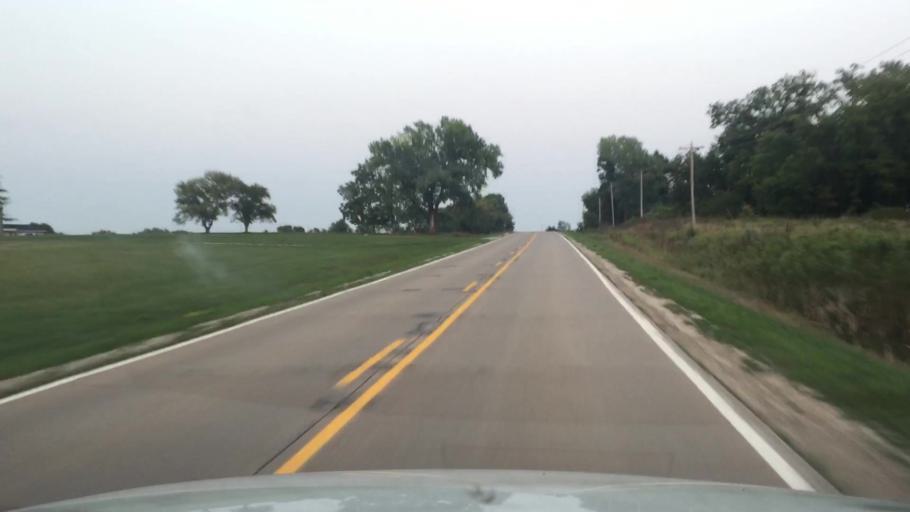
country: US
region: Iowa
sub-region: Clarke County
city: Osceola
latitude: 41.1909
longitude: -93.6658
